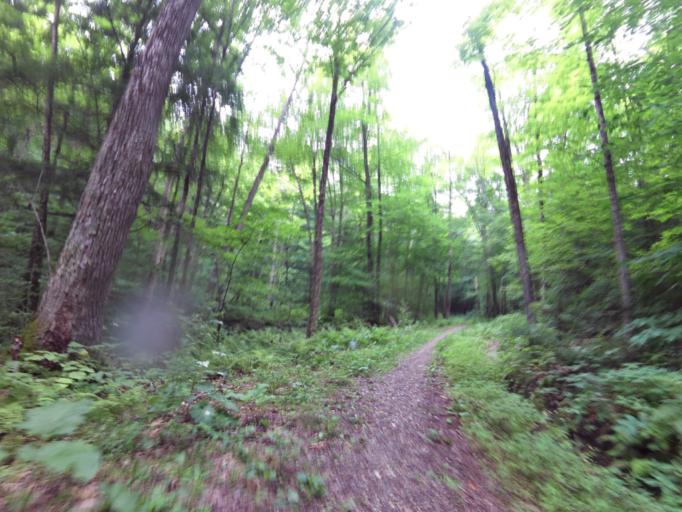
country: CA
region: Quebec
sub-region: Outaouais
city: Wakefield
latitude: 45.6110
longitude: -76.0479
